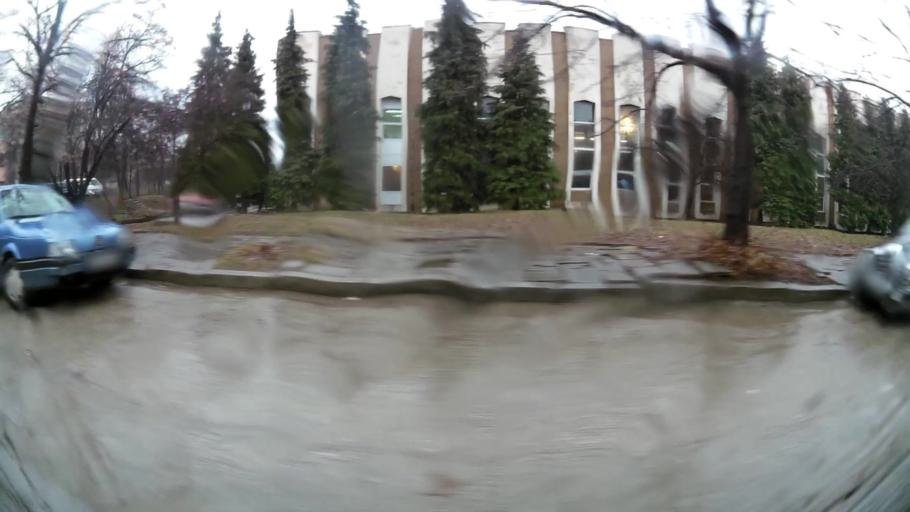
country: BG
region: Sofia-Capital
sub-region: Stolichna Obshtina
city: Sofia
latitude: 42.6582
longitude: 23.3548
